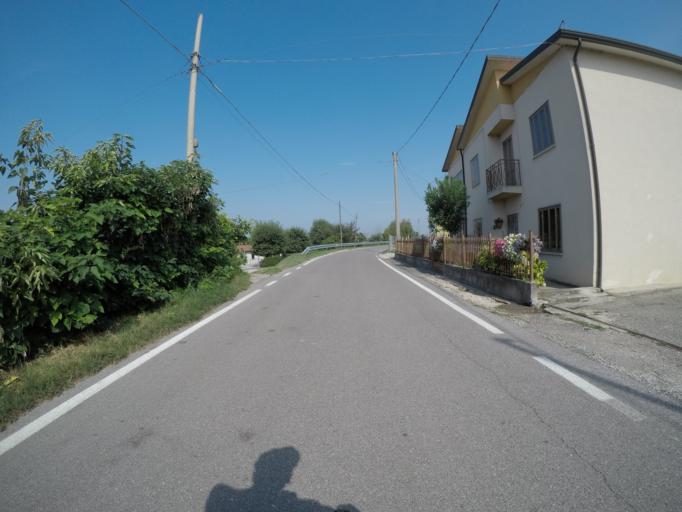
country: IT
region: Veneto
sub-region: Provincia di Rovigo
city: Lendinara
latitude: 45.0656
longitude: 11.6132
